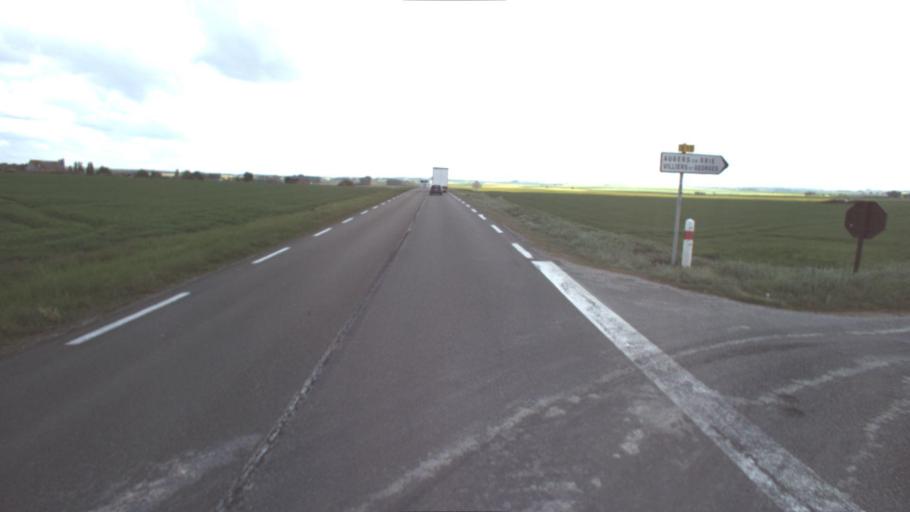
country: FR
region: Ile-de-France
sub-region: Departement de Seine-et-Marne
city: Villiers-Saint-Georges
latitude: 48.6909
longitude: 3.3383
